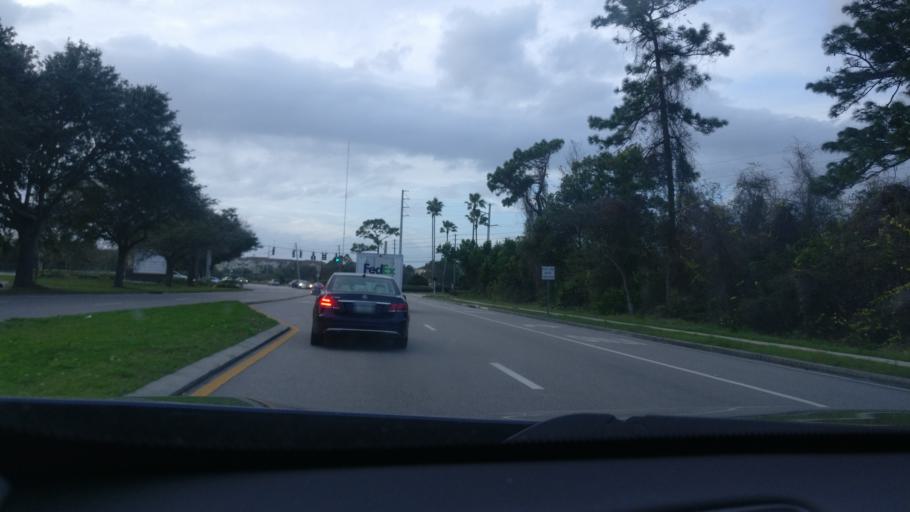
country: US
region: Florida
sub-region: Volusia County
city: DeBary
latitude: 28.9115
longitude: -81.2944
